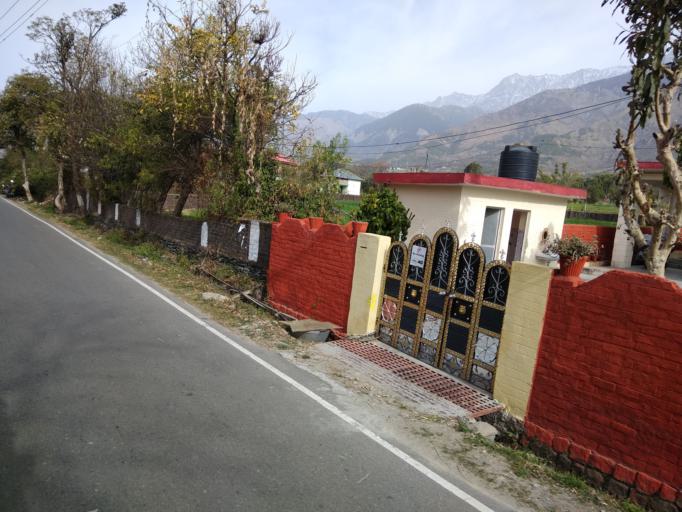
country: IN
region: Himachal Pradesh
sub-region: Kangra
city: Dharmsala
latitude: 32.1672
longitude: 76.3925
